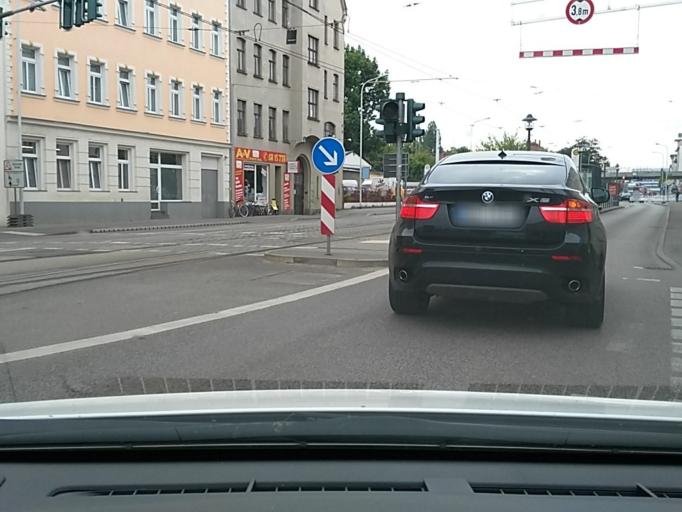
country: DE
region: Saxony-Anhalt
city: Halle (Saale)
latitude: 51.4791
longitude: 11.9946
